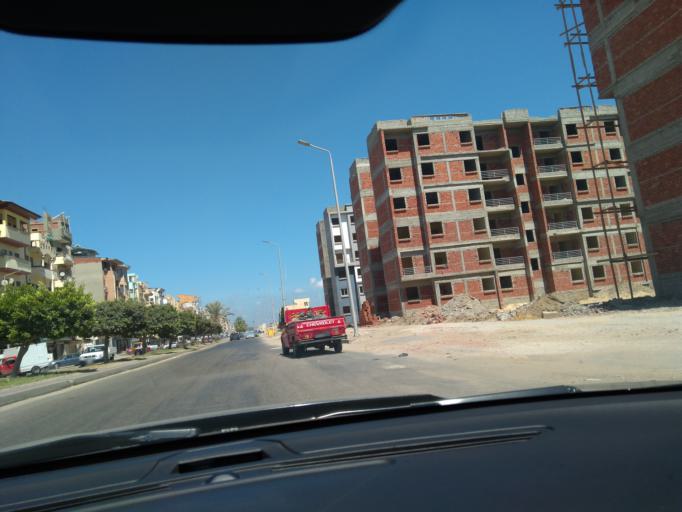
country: EG
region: Dumyat
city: Faraskur
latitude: 31.4250
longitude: 31.6762
